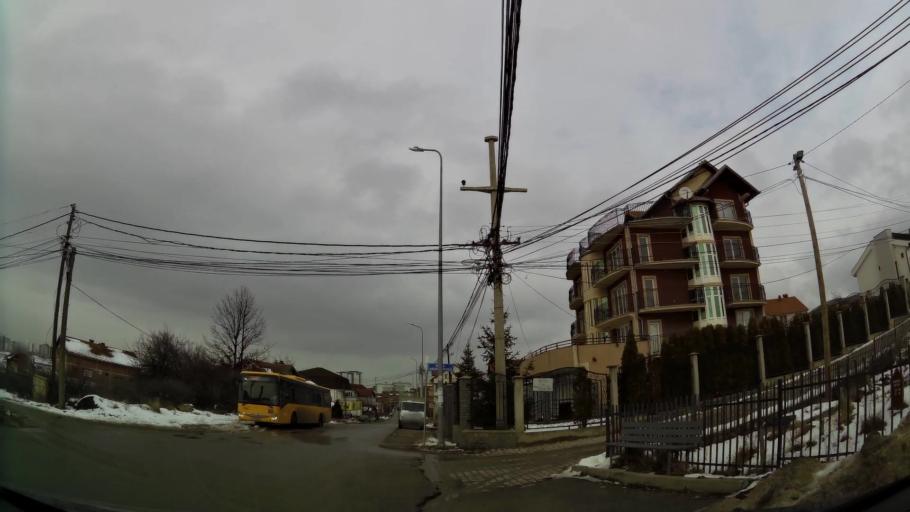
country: XK
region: Pristina
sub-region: Komuna e Prishtines
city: Pristina
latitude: 42.6477
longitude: 21.1951
